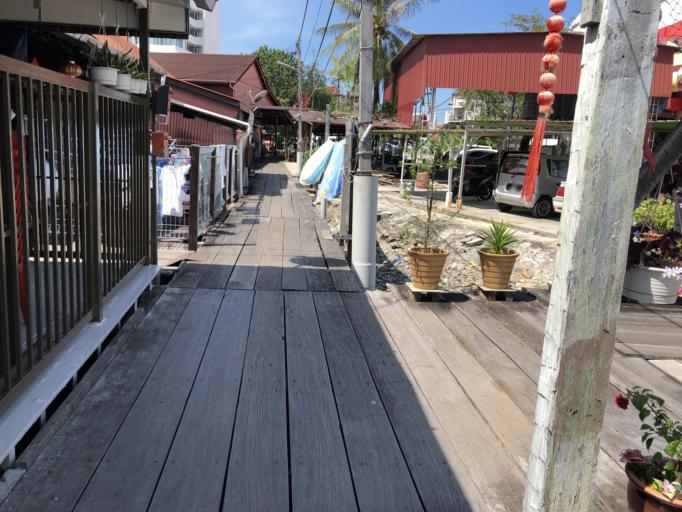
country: MY
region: Penang
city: George Town
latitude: 5.4131
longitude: 100.3414
